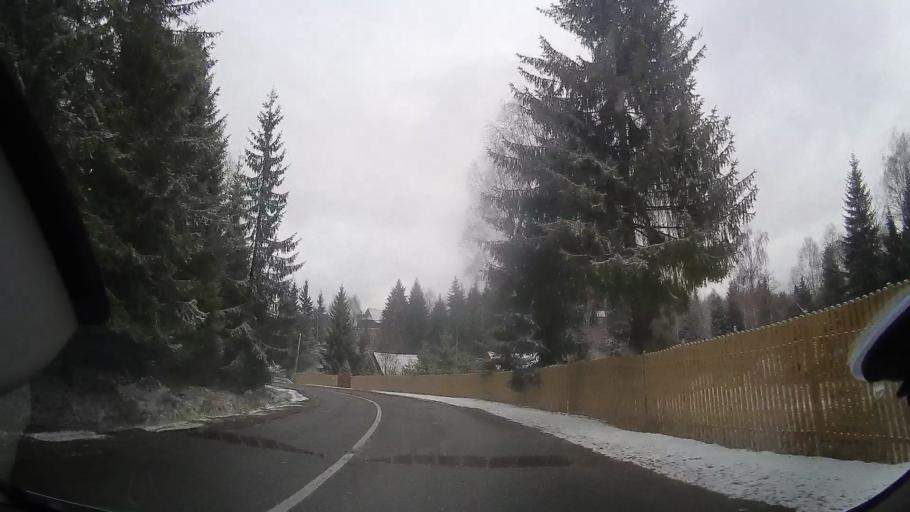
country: RO
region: Cluj
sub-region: Comuna Calatele
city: Calatele
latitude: 46.7154
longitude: 23.0441
